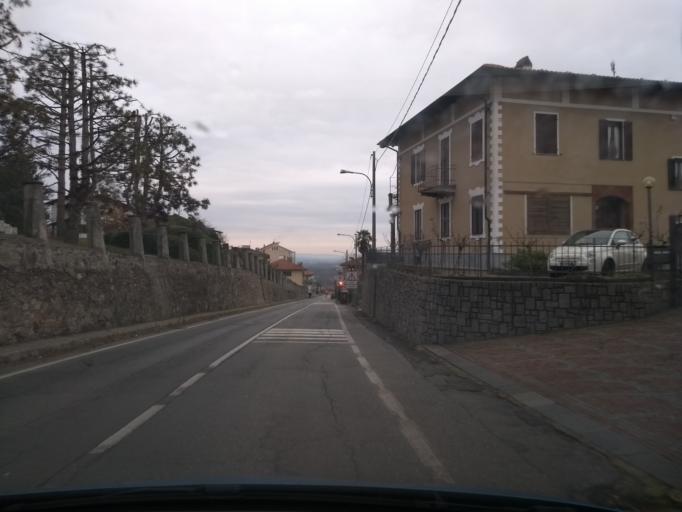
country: IT
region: Piedmont
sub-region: Provincia di Torino
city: Parella
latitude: 45.4305
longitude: 7.7891
